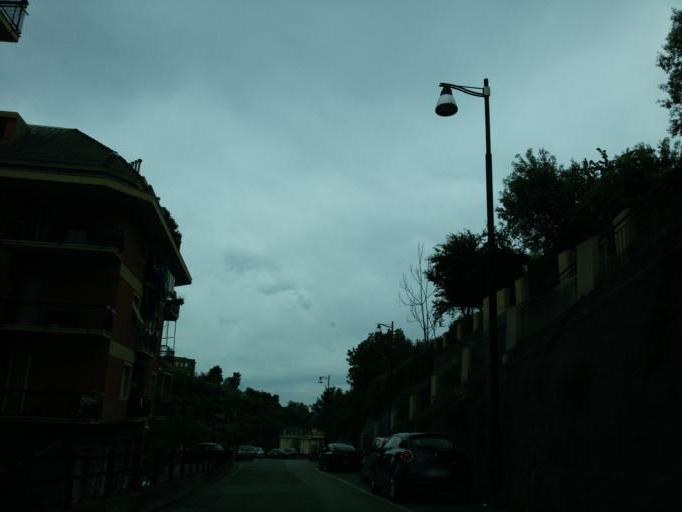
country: IT
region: Liguria
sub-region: Provincia di Genova
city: San Teodoro
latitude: 44.4206
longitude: 8.8977
